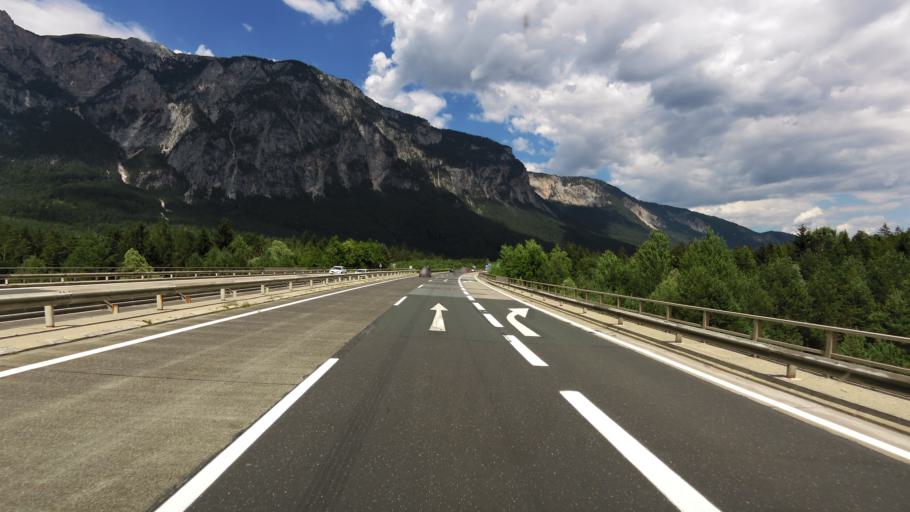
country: AT
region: Carinthia
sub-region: Politischer Bezirk Villach Land
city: Hohenthurn
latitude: 46.5663
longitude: 13.6887
